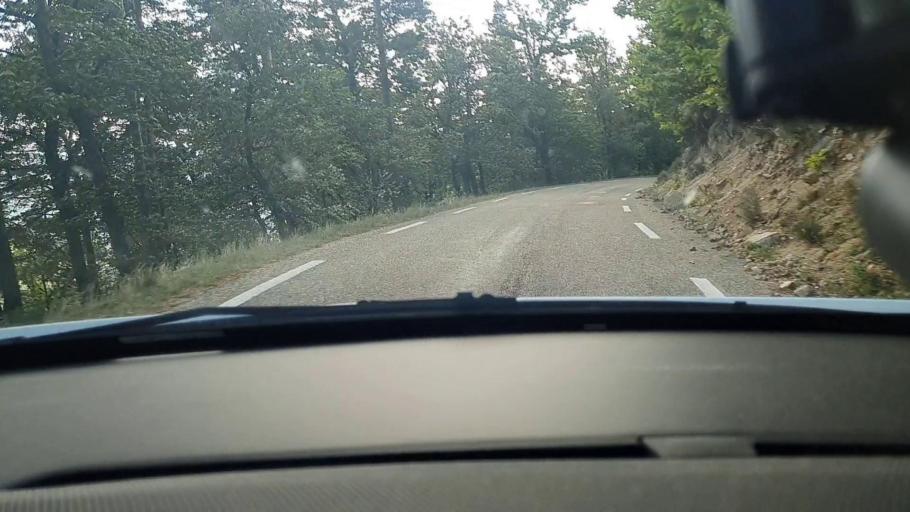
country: FR
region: Languedoc-Roussillon
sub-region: Departement du Gard
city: Branoux-les-Taillades
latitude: 44.3632
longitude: 3.9239
